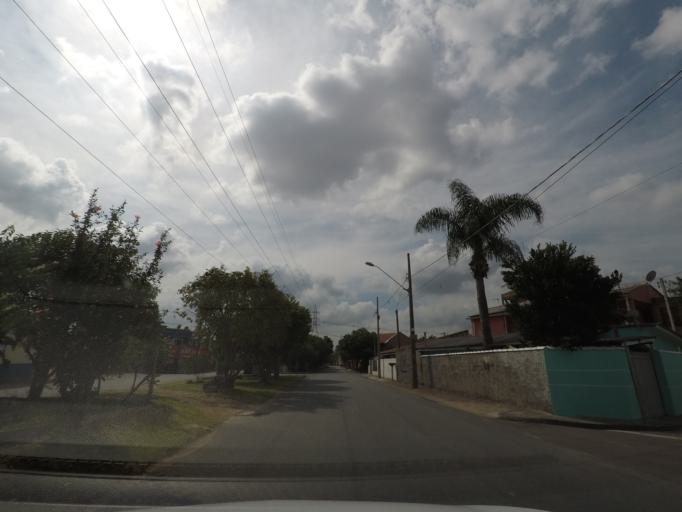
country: BR
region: Parana
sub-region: Pinhais
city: Pinhais
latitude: -25.4654
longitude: -49.1967
